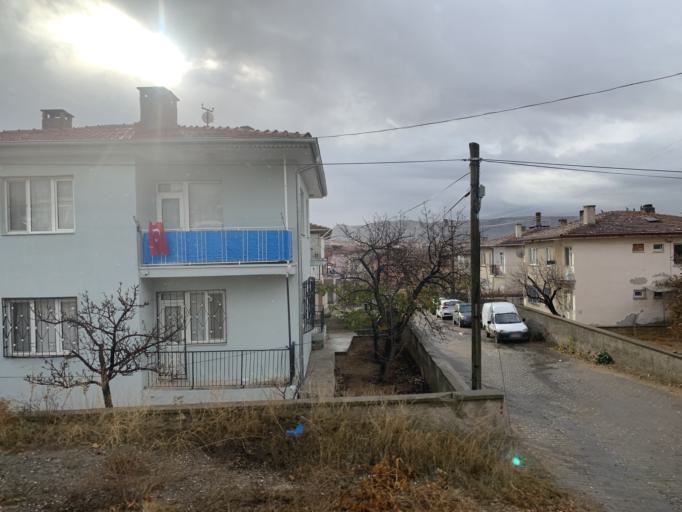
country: TR
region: Nevsehir
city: Avanos
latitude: 38.7207
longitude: 34.8580
